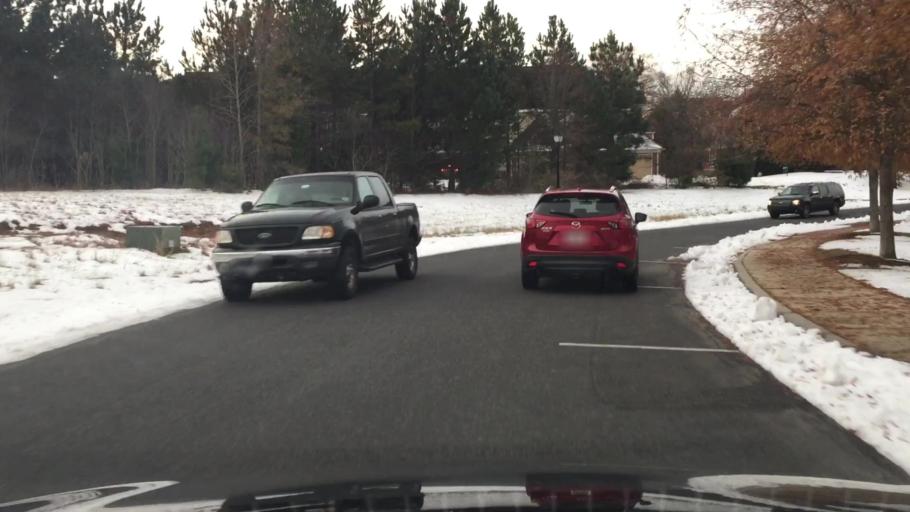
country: US
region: North Carolina
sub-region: Mecklenburg County
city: Cornelius
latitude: 35.5006
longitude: -80.8591
